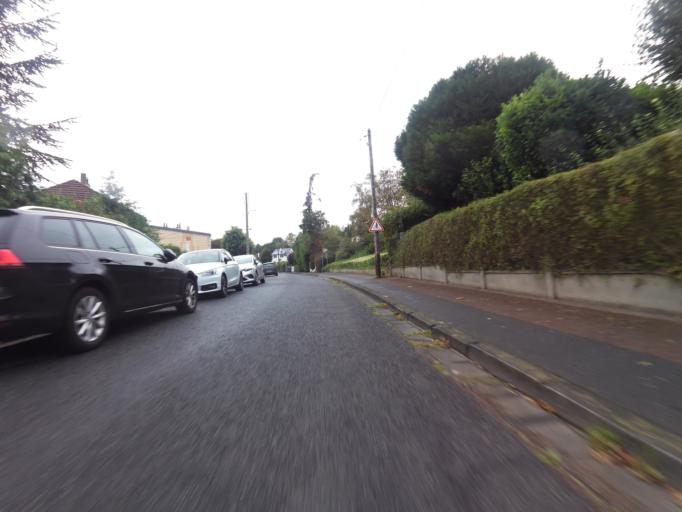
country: FR
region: Lower Normandy
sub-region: Departement du Calvados
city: Caen
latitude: 49.1946
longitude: -0.3543
